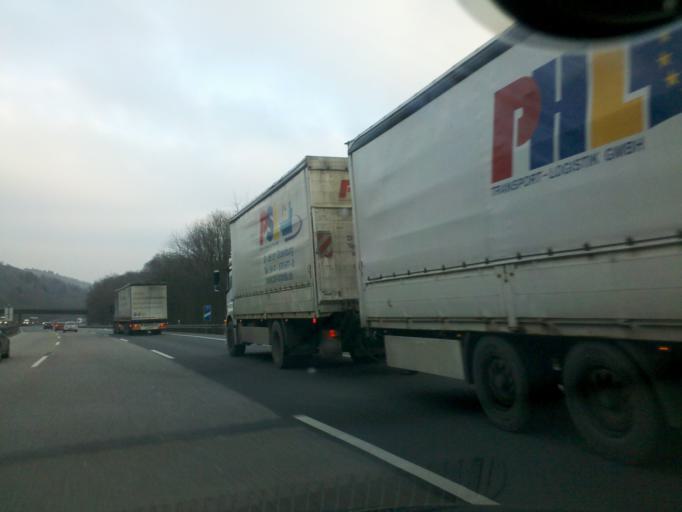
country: DE
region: North Rhine-Westphalia
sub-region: Regierungsbezirk Arnsberg
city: Siegen
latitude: 50.8328
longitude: 8.0305
